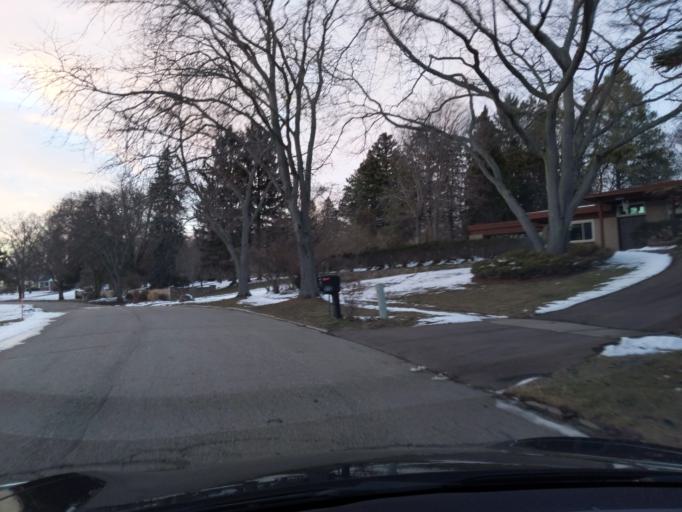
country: US
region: Michigan
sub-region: Ingham County
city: Okemos
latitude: 42.7176
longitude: -84.4353
